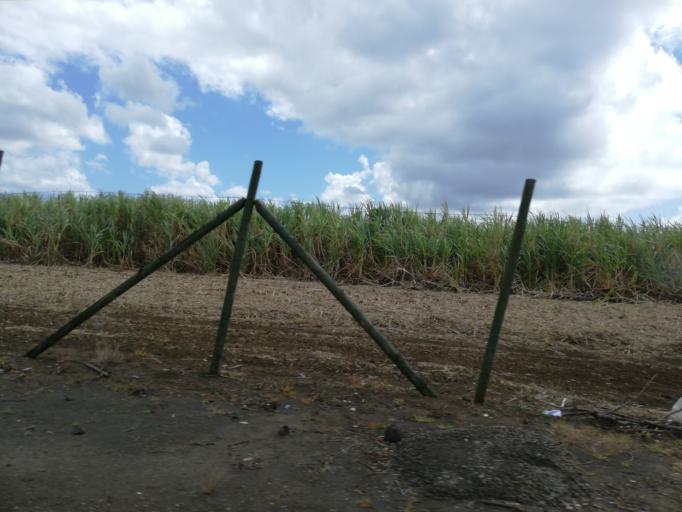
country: MU
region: Riviere du Rempart
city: Esperance Trebuchet
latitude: -20.0721
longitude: 57.6652
